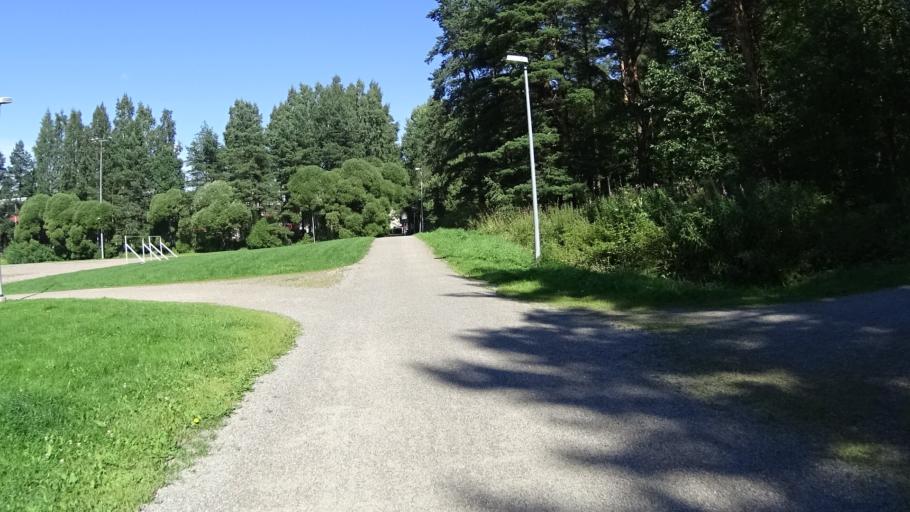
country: FI
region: Uusimaa
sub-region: Helsinki
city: Teekkarikylae
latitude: 60.2370
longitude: 24.8685
